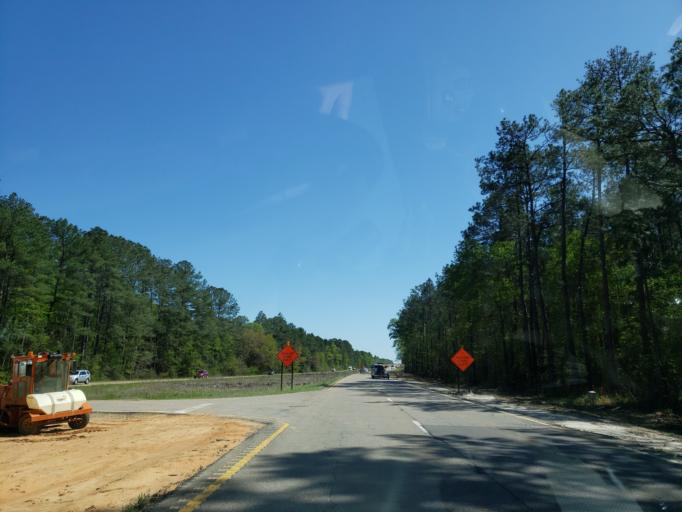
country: US
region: Mississippi
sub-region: Lamar County
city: Purvis
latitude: 31.1025
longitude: -89.2162
